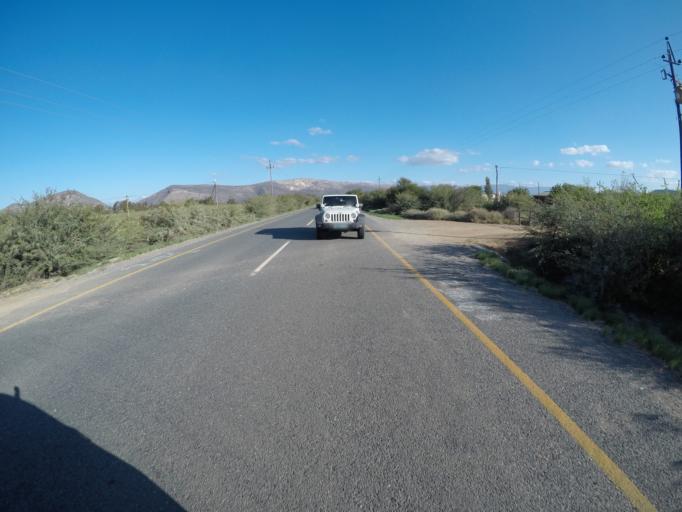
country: ZA
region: Western Cape
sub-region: Cape Winelands District Municipality
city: Ashton
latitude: -33.8016
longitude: 19.7816
